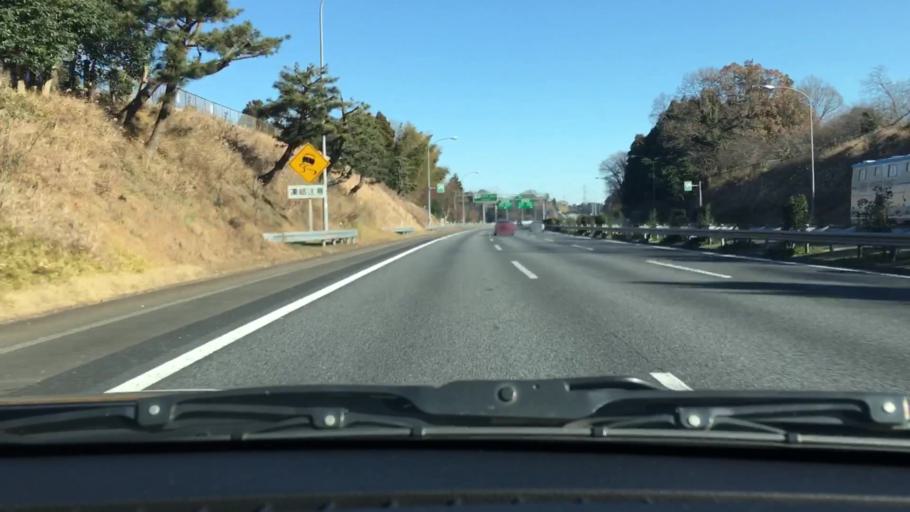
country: JP
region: Chiba
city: Narita
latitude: 35.7644
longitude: 140.3253
